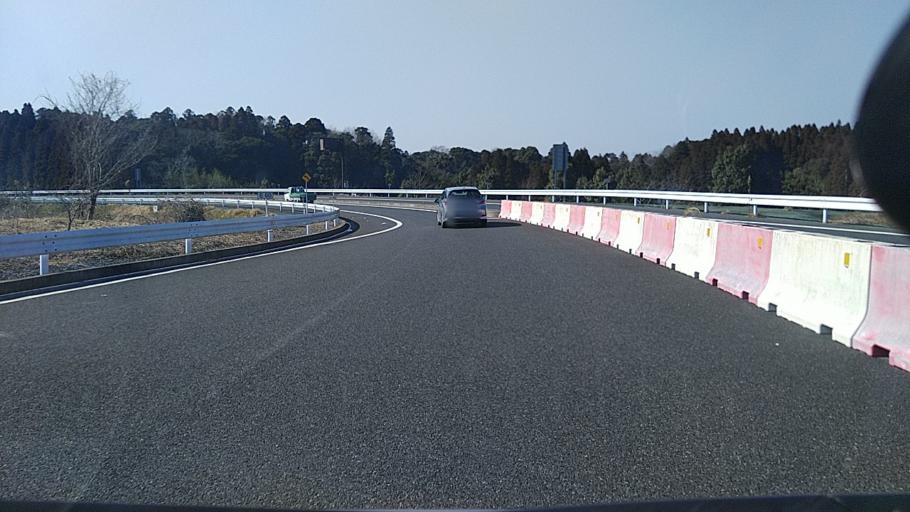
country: JP
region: Chiba
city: Mobara
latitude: 35.4042
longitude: 140.2462
